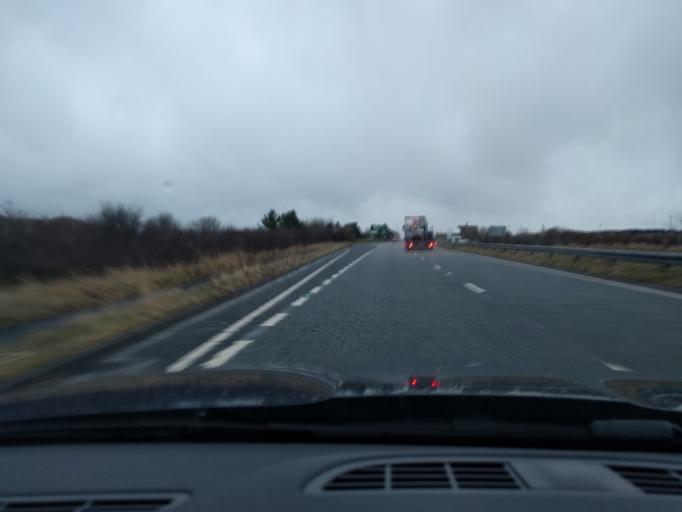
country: GB
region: England
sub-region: Northumberland
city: Berwick-Upon-Tweed
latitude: 55.7899
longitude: -2.0217
